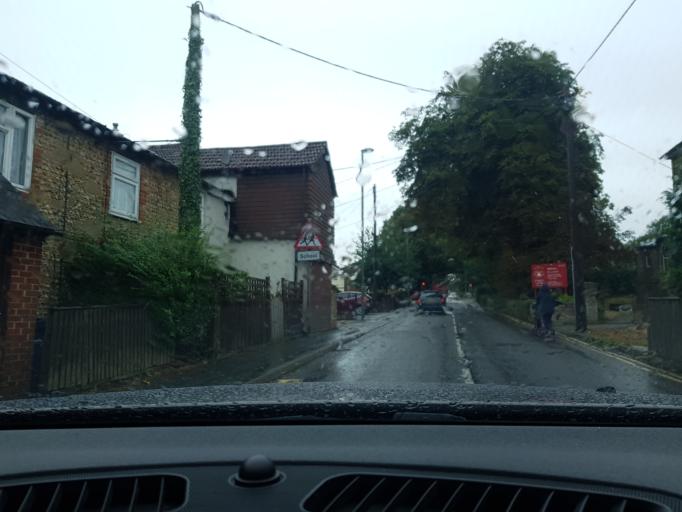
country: GB
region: England
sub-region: Surrey
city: Hale
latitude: 51.2343
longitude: -0.7996
